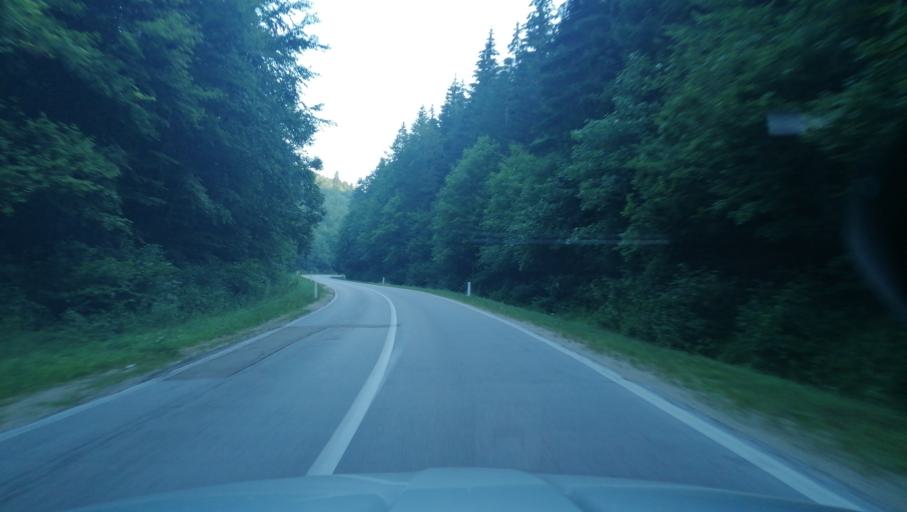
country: BA
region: Federation of Bosnia and Herzegovina
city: Prozor
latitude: 43.8744
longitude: 17.5934
